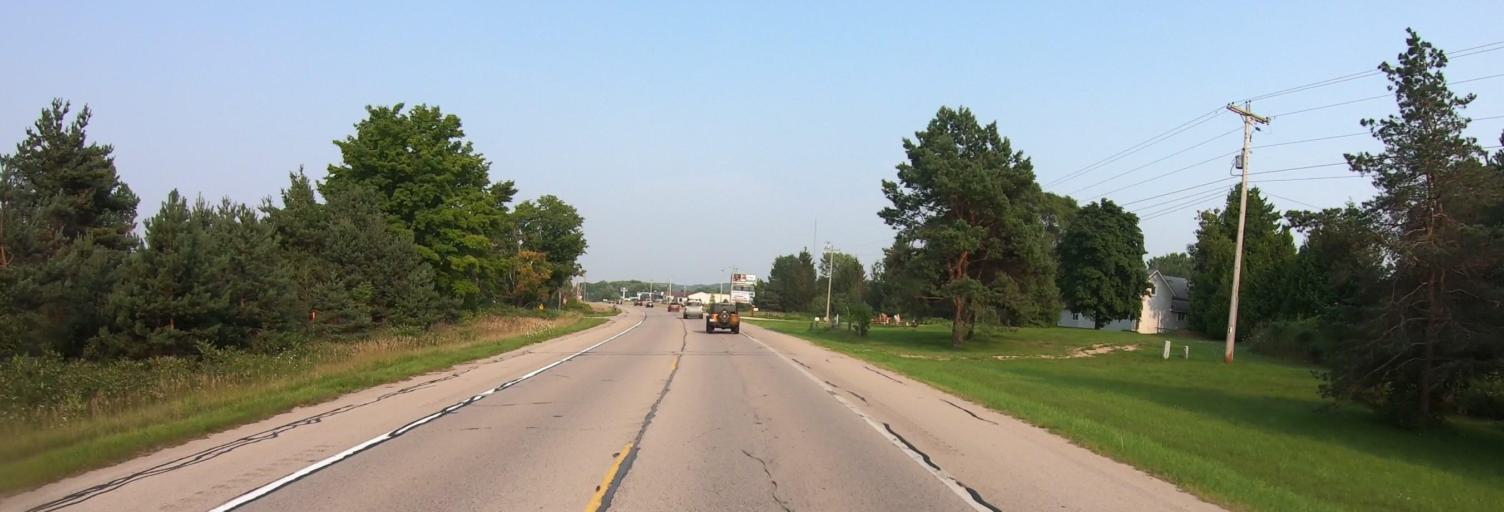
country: US
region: Michigan
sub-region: Emmet County
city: Harbor Springs
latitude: 45.3616
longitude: -85.1088
